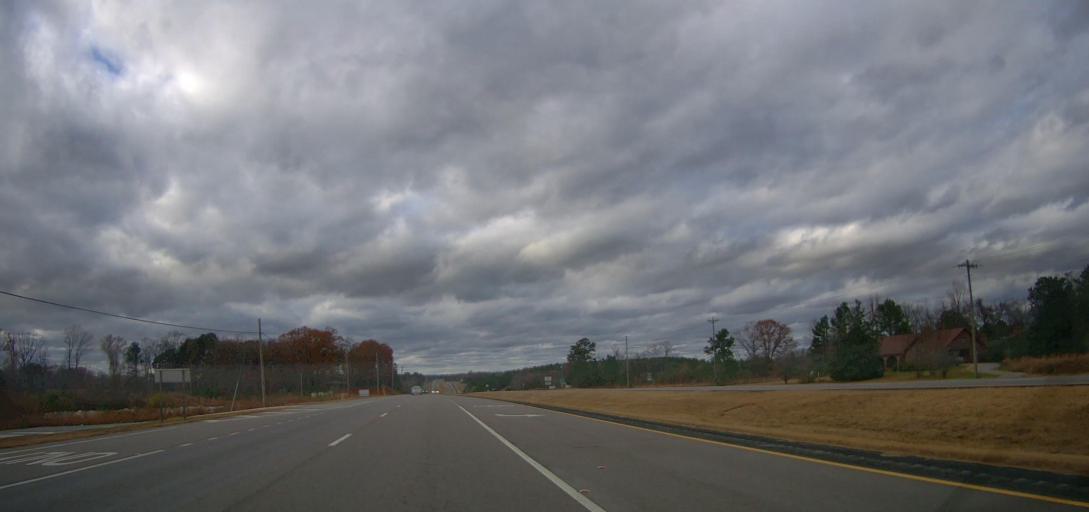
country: US
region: Alabama
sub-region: Cullman County
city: Cullman
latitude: 34.2433
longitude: -86.9583
